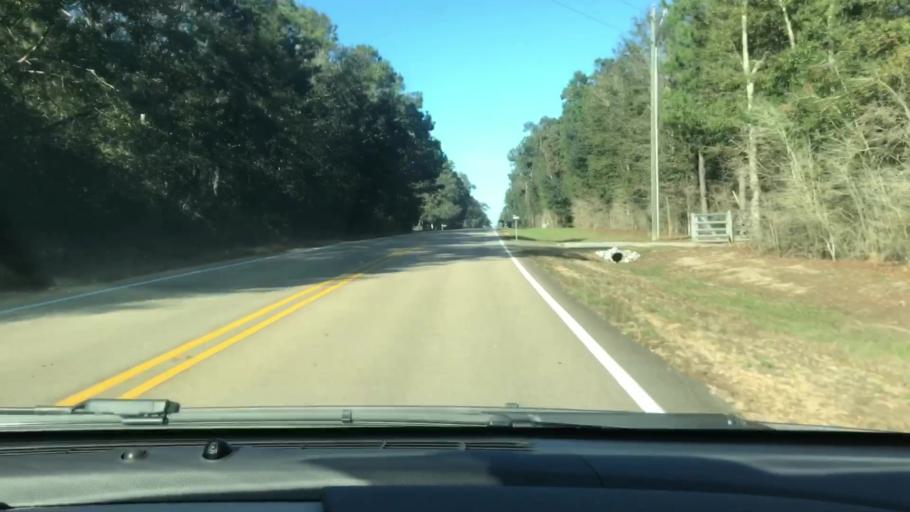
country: US
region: Louisiana
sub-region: Saint Tammany Parish
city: Abita Springs
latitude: 30.5510
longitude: -90.0448
